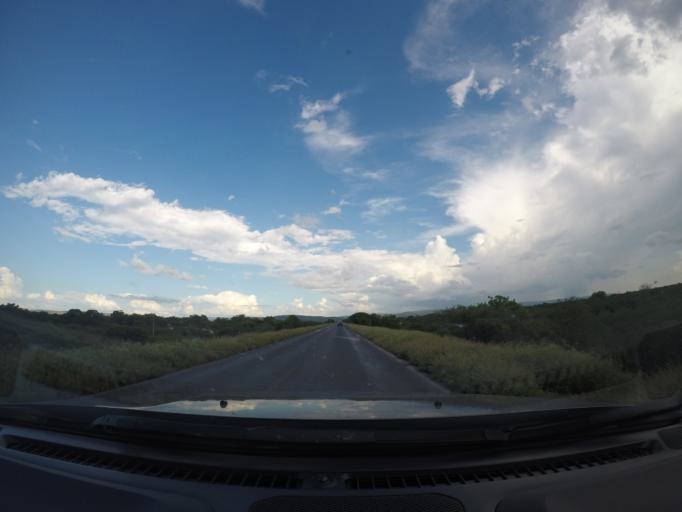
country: BR
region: Bahia
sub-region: Ibotirama
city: Ibotirama
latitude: -12.1750
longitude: -43.2535
